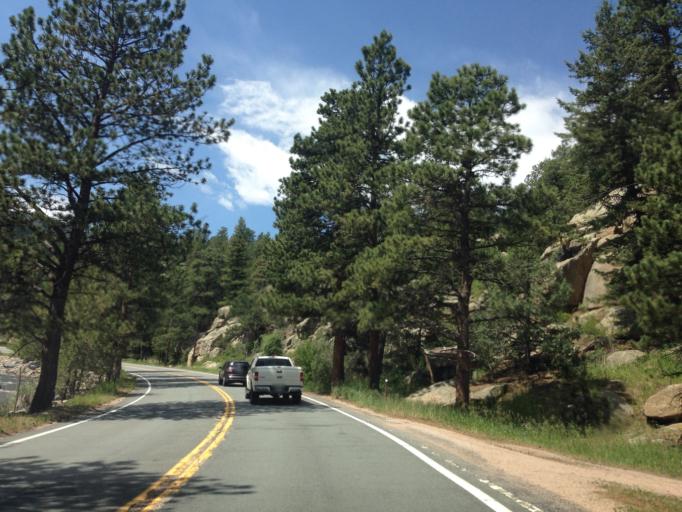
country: US
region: Colorado
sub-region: Larimer County
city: Estes Park
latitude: 40.3939
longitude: -105.4483
